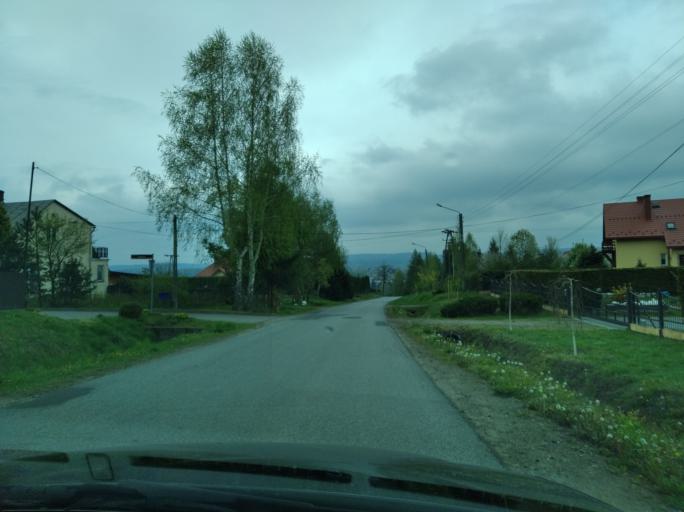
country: PL
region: Subcarpathian Voivodeship
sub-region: Powiat sanocki
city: Sanok
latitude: 49.5582
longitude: 22.2323
